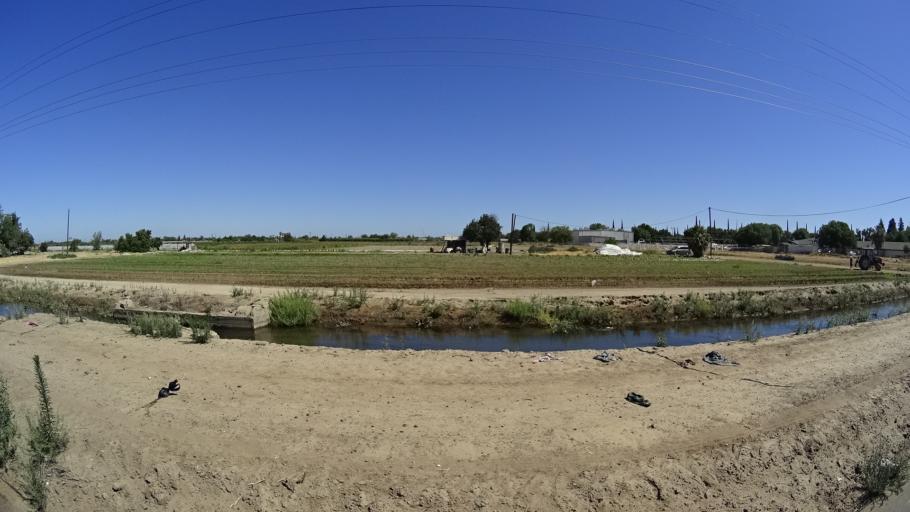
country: US
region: California
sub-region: Fresno County
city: West Park
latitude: 36.6995
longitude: -119.8027
